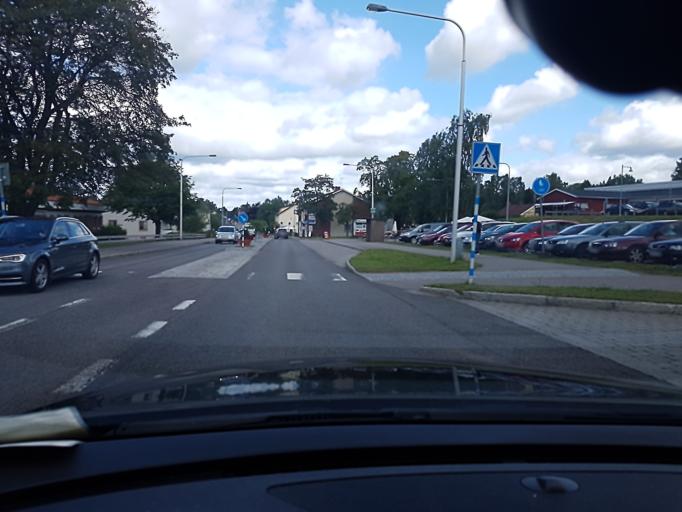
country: SE
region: Kronoberg
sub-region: Lessebo Kommun
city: Lessebo
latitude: 56.7518
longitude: 15.2697
